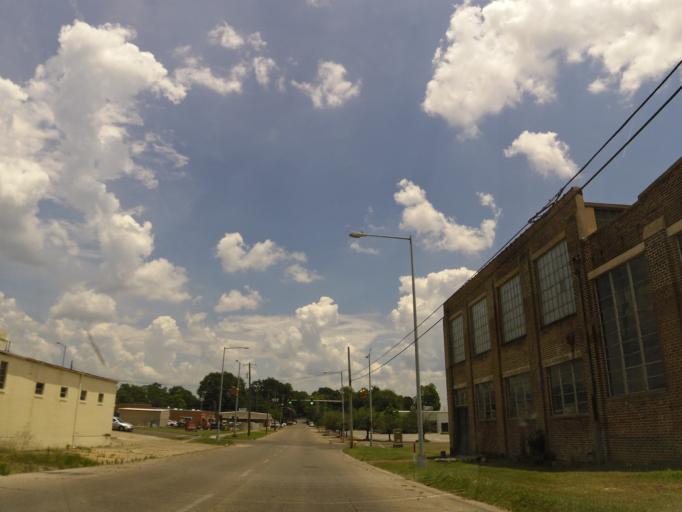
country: US
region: Mississippi
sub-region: Lauderdale County
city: Meridian
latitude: 32.3658
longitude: -88.6968
